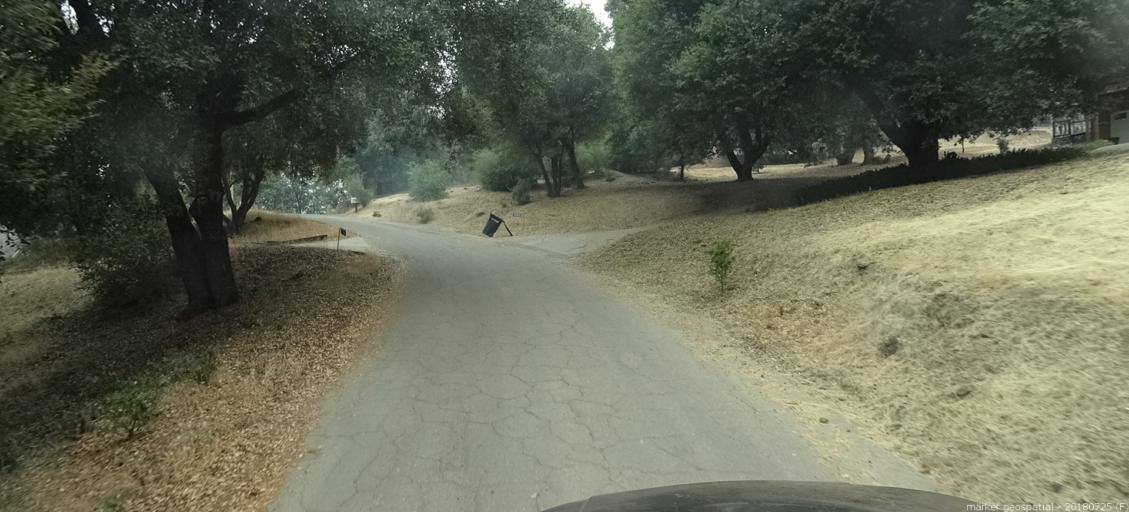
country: US
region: California
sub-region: Madera County
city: Oakhurst
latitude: 37.3654
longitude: -119.6007
